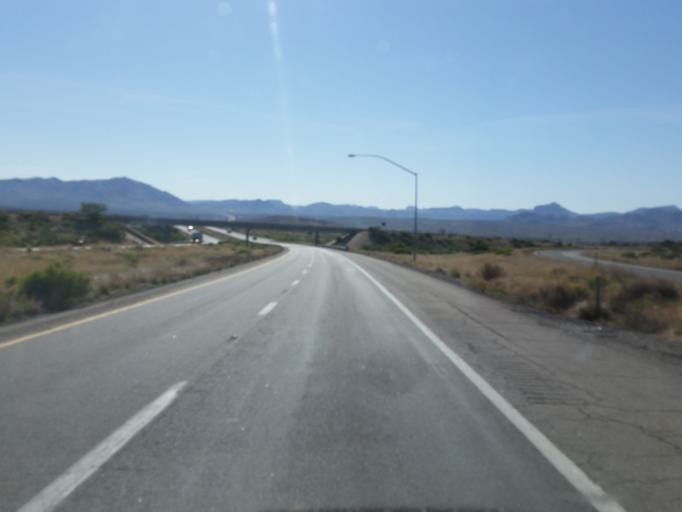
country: US
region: Arizona
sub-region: Mohave County
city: New Kingman-Butler
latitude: 35.1593
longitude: -113.6992
